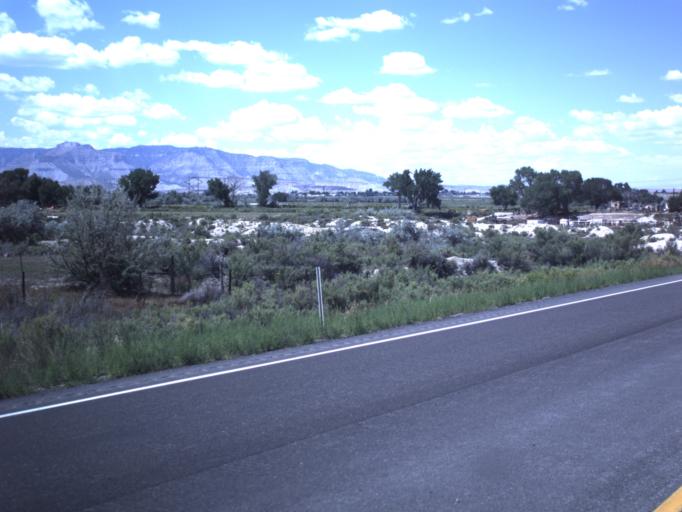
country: US
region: Utah
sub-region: Emery County
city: Huntington
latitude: 39.2955
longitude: -110.9660
